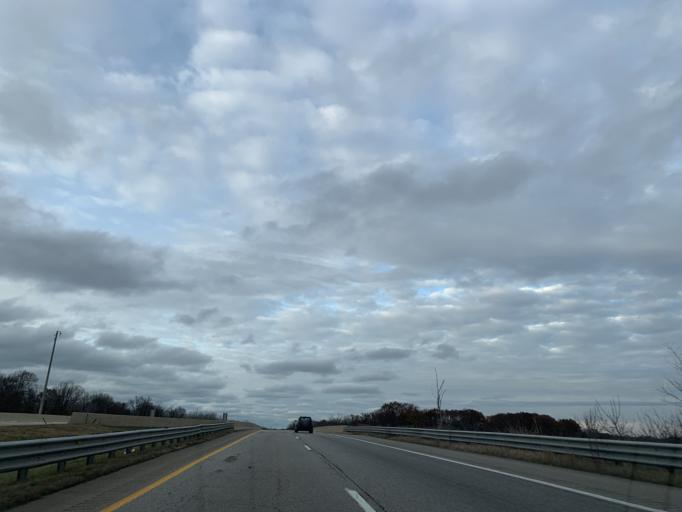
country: US
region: Michigan
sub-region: Berrien County
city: Benton Heights
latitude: 42.1335
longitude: -86.3680
